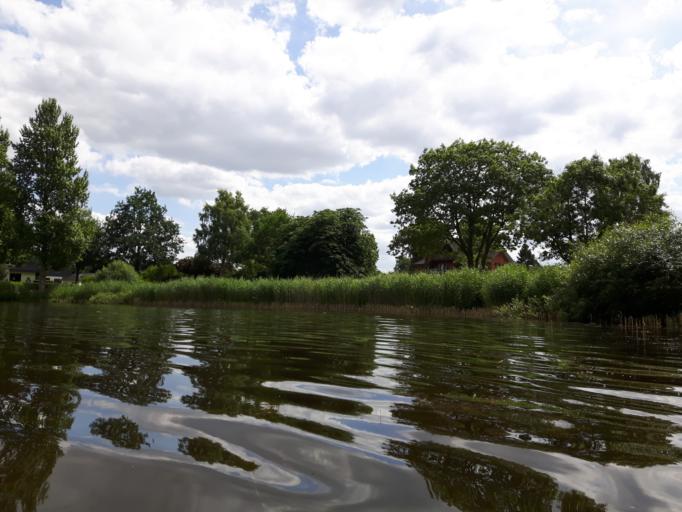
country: DE
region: Schleswig-Holstein
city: Muhbrook
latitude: 54.1316
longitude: 9.9885
